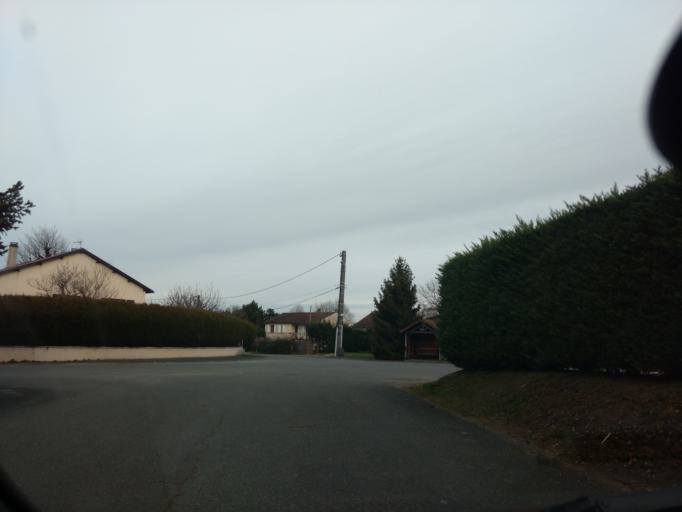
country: FR
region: Midi-Pyrenees
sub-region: Departement de l'Aveyron
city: Villeneuve
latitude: 44.3978
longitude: 2.0772
